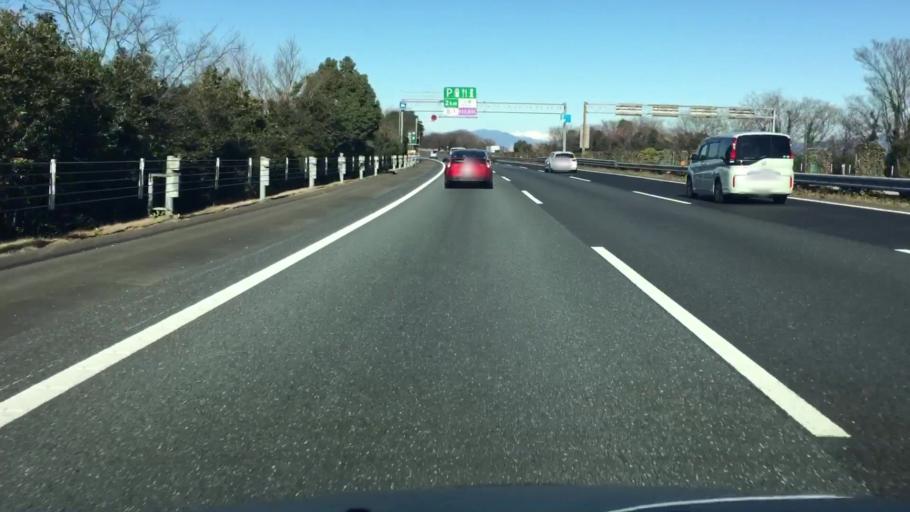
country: JP
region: Saitama
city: Honjo
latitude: 36.2420
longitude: 139.1444
